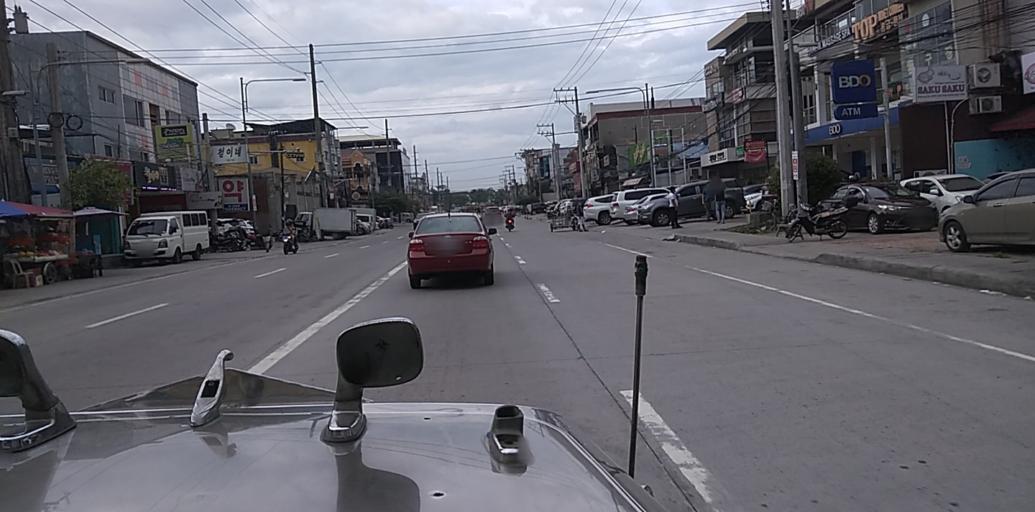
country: PH
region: Central Luzon
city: Santol
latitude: 15.1599
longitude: 120.5564
